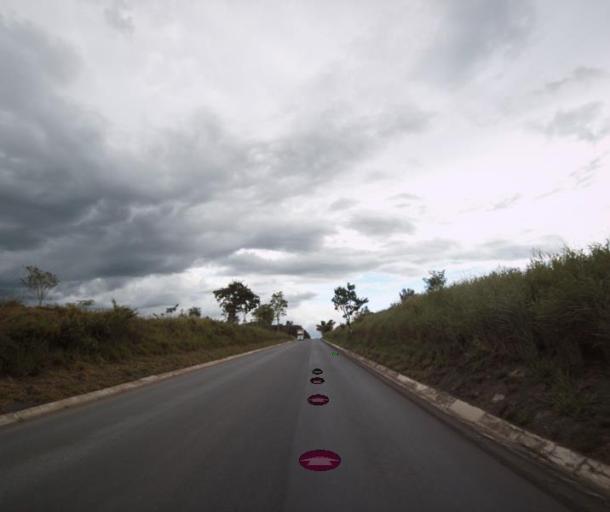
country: BR
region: Goias
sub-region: Itapaci
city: Itapaci
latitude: -14.9989
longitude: -49.4101
